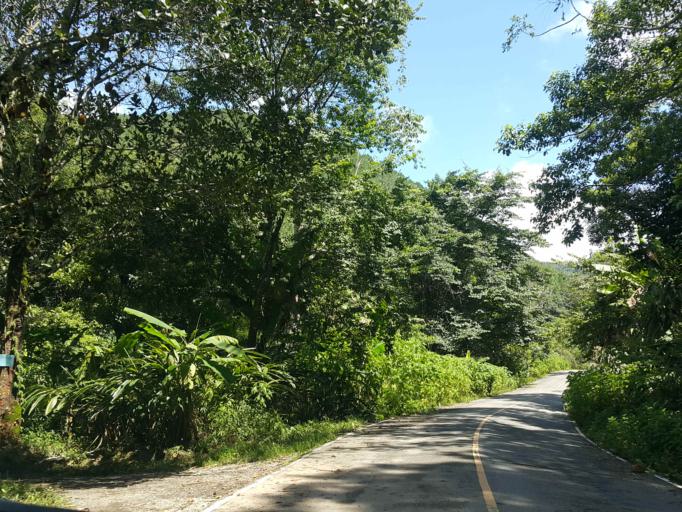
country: TH
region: Chiang Mai
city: Mae Chaem
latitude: 18.5255
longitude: 98.5220
